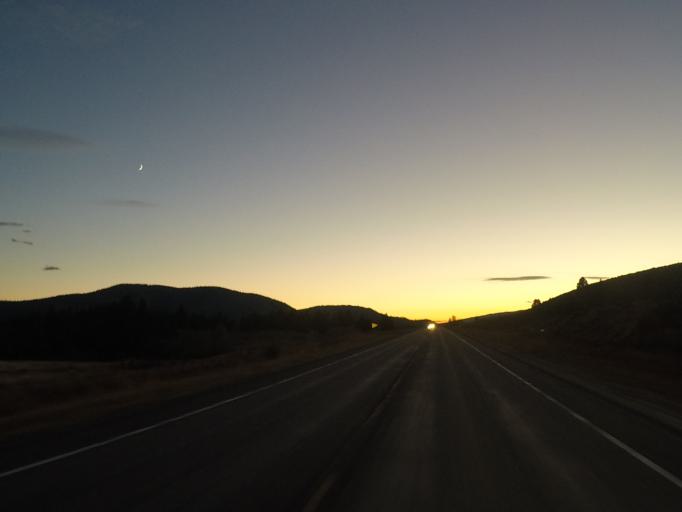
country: US
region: Montana
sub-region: Missoula County
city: Seeley Lake
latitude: 47.0422
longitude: -113.2165
